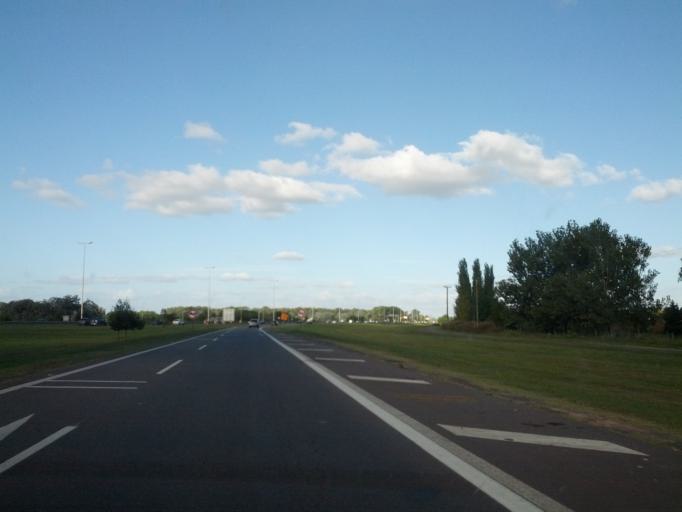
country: AR
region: Buenos Aires
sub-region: Partido de Lujan
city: Lujan
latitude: -34.5692
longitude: -59.0613
